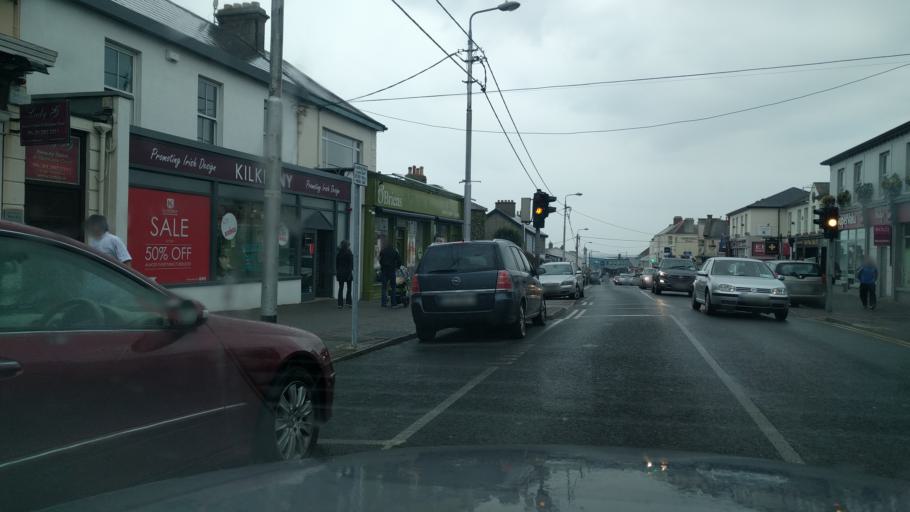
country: IE
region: Leinster
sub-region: Wicklow
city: Greystones
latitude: 53.1452
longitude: -6.0638
